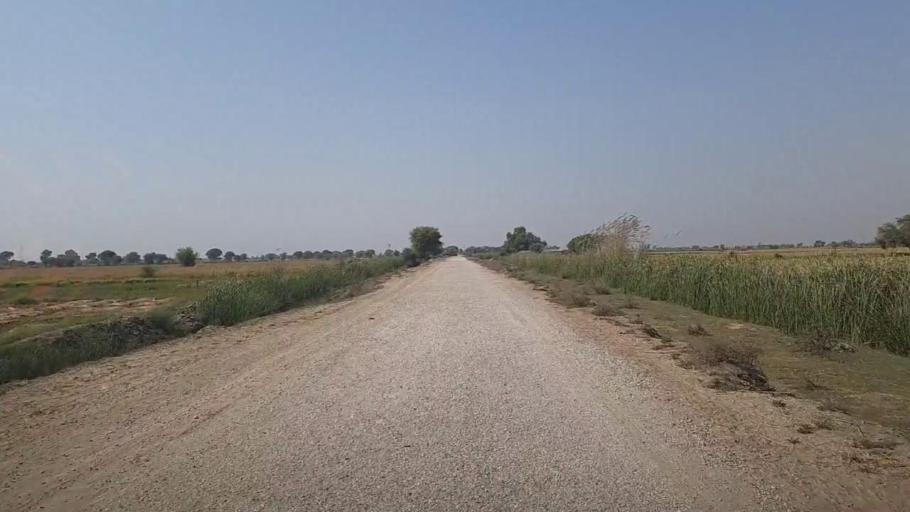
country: PK
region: Sindh
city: Kandhkot
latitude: 28.3920
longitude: 69.2827
